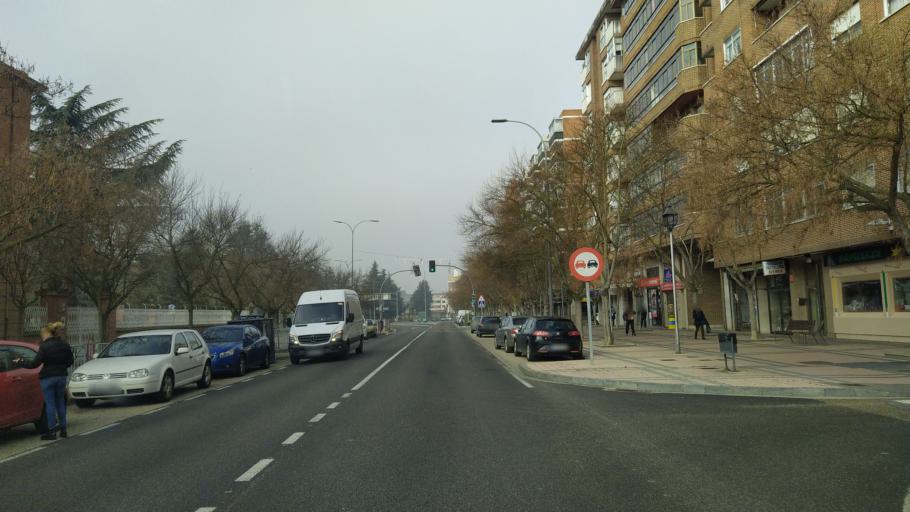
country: ES
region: Castille and Leon
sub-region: Provincia de Palencia
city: Palencia
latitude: 41.9977
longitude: -4.5220
